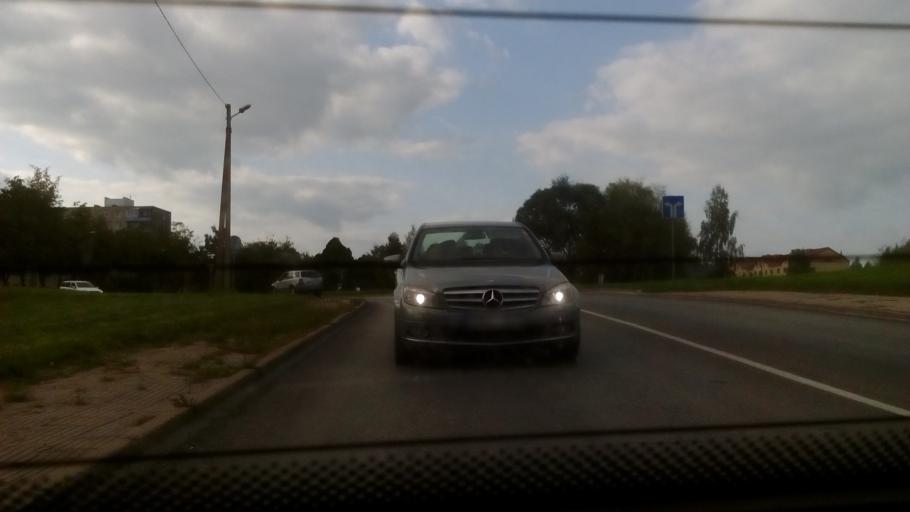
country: LT
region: Alytaus apskritis
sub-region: Alytus
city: Alytus
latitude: 54.4098
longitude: 24.0265
